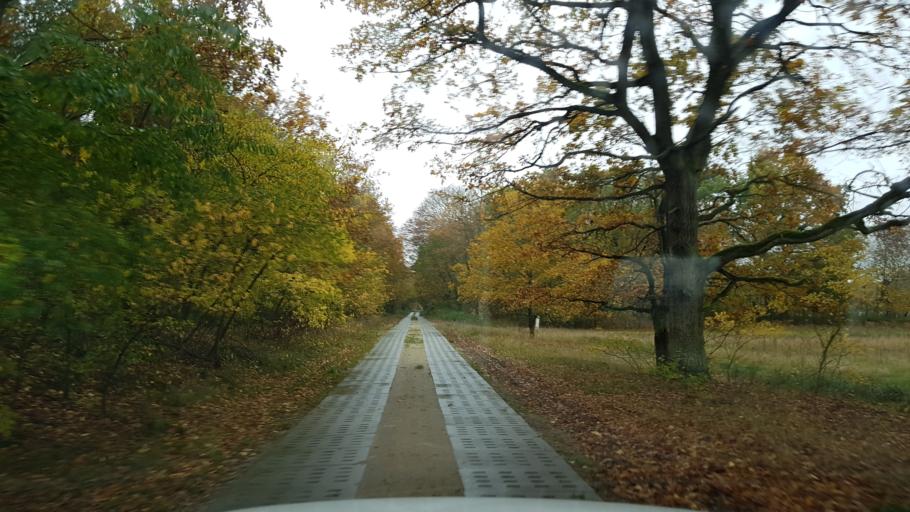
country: PL
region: West Pomeranian Voivodeship
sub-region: Powiat goleniowski
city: Goleniow
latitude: 53.5820
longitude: 14.7712
